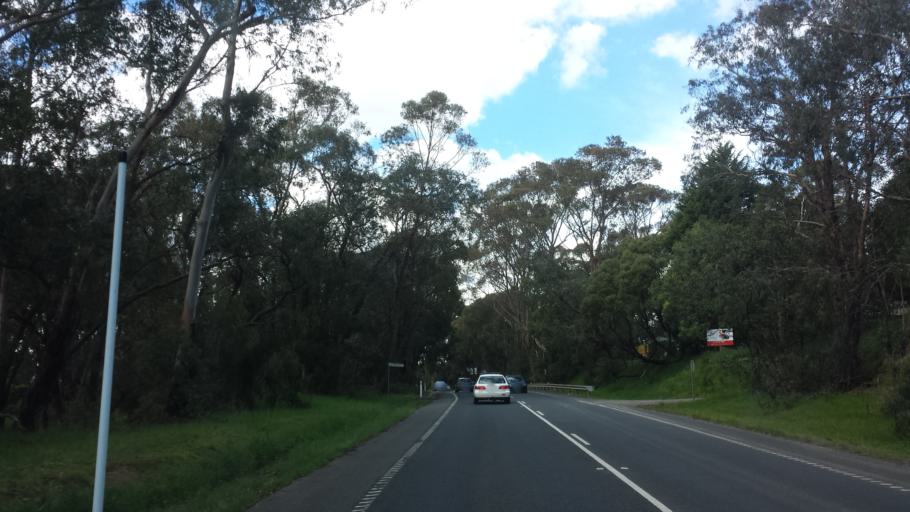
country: AU
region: Victoria
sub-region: Yarra Ranges
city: Selby
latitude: -37.9589
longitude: 145.3763
